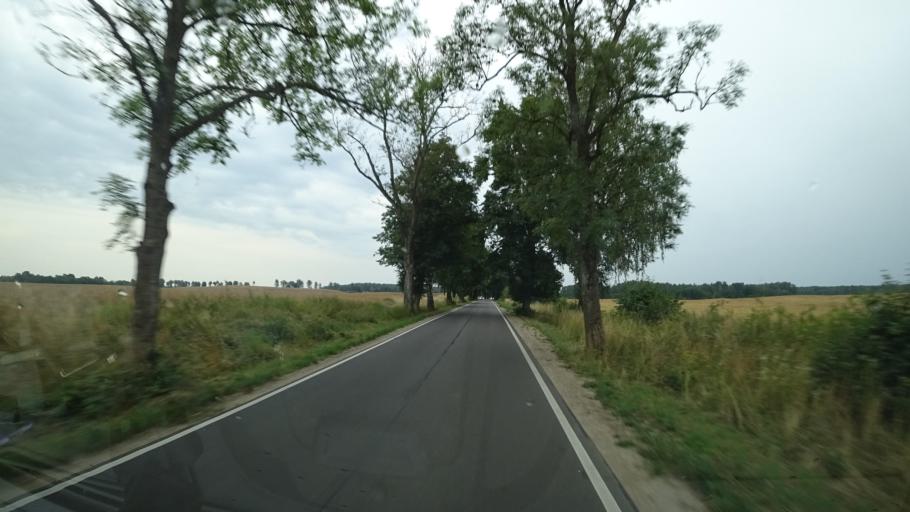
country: PL
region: Warmian-Masurian Voivodeship
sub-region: Powiat gizycki
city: Ryn
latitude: 53.9084
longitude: 21.5618
